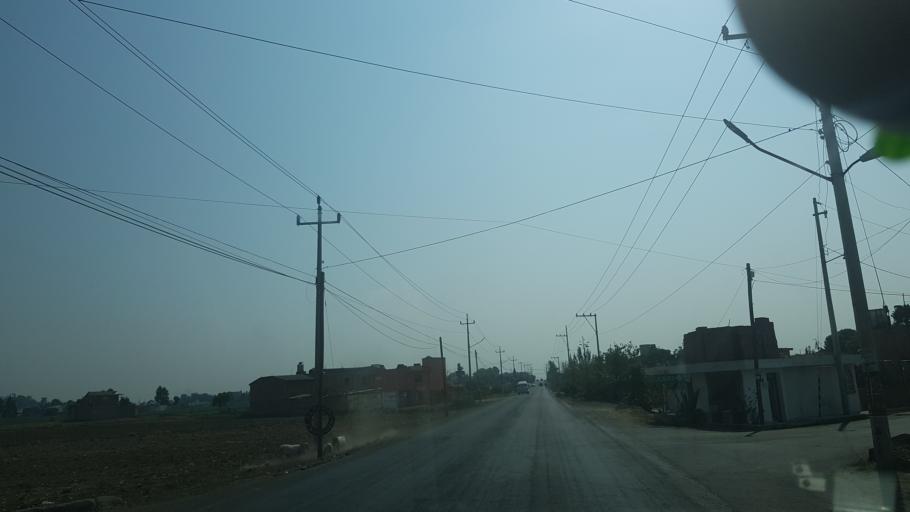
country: MX
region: Puebla
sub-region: San Jeronimo Tecuanipan
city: Los Reyes Tlanechicolpan
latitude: 19.0533
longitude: -98.3409
